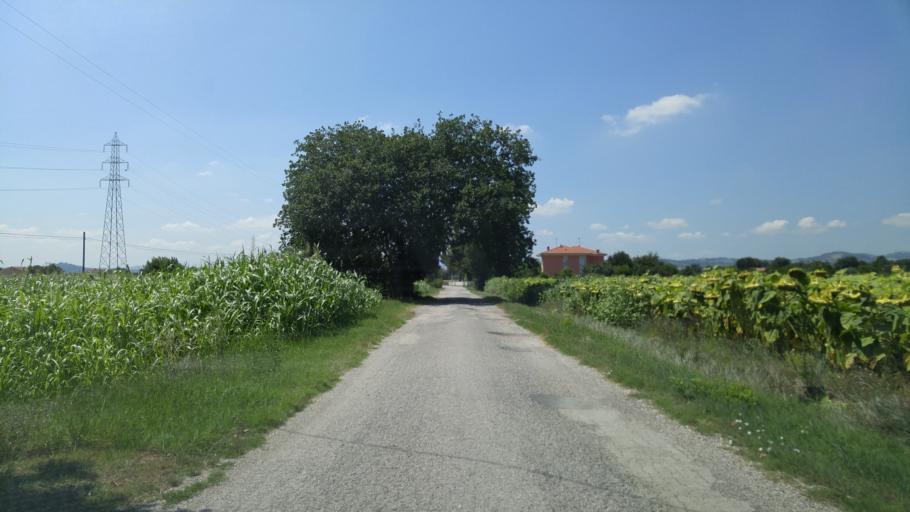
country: IT
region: The Marches
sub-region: Provincia di Pesaro e Urbino
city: Cuccurano
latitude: 43.7935
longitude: 12.9675
